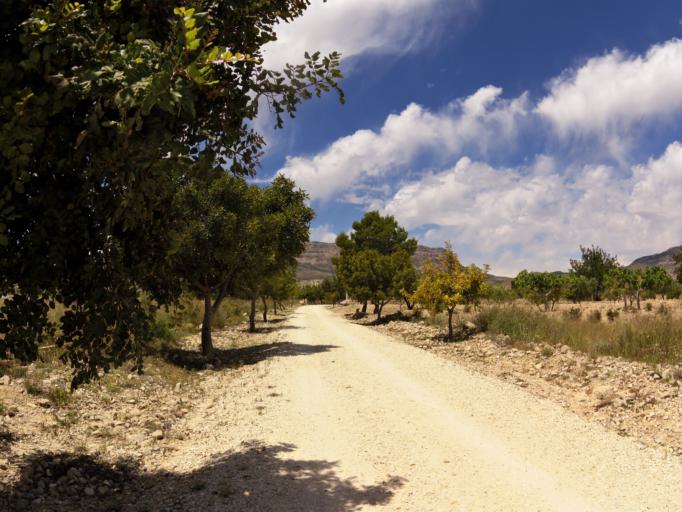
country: ES
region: Valencia
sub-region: Provincia de Alicante
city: Agost
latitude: 38.4447
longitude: -0.6646
